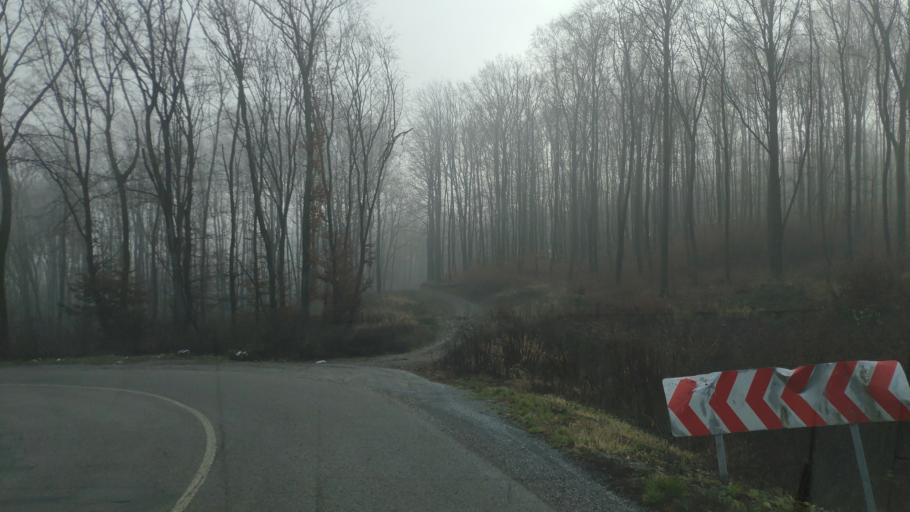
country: SK
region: Kosicky
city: Kosice
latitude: 48.7066
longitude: 21.3813
